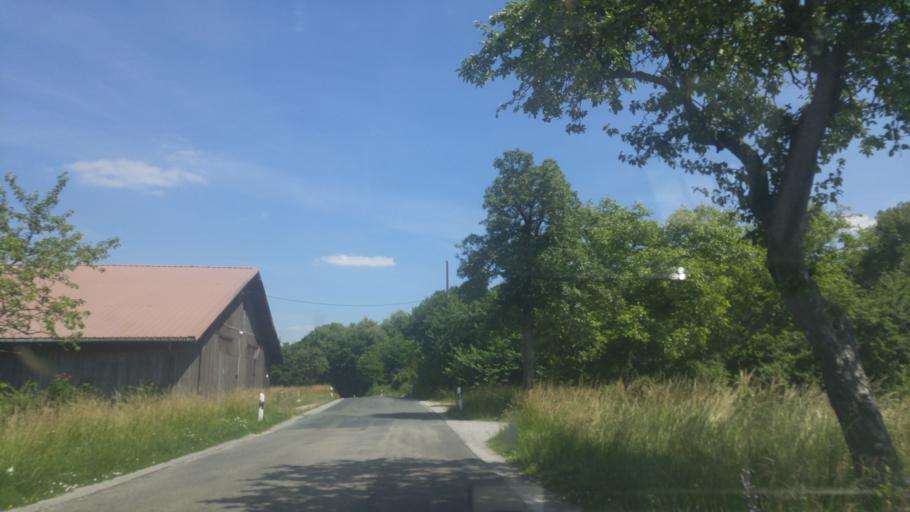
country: DE
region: Bavaria
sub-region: Regierungsbezirk Mittelfranken
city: Hagenbuchach
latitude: 49.5366
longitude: 10.7465
